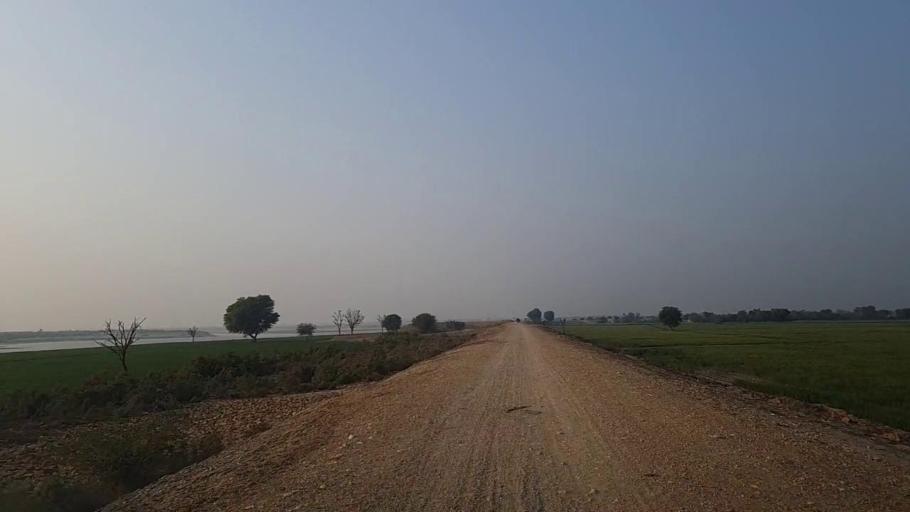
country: PK
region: Sindh
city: Sann
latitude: 26.1291
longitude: 68.1401
